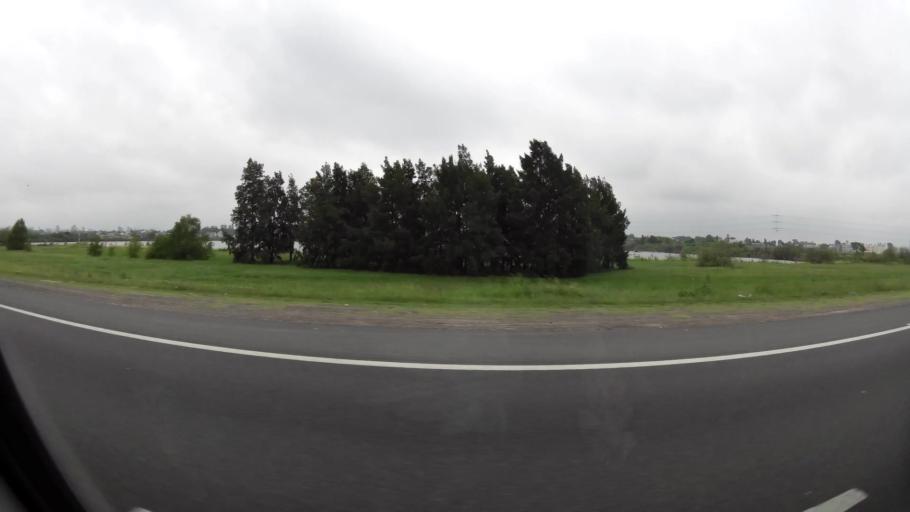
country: AR
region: Buenos Aires
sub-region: Partido de Quilmes
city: Quilmes
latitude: -34.7334
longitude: -58.2157
